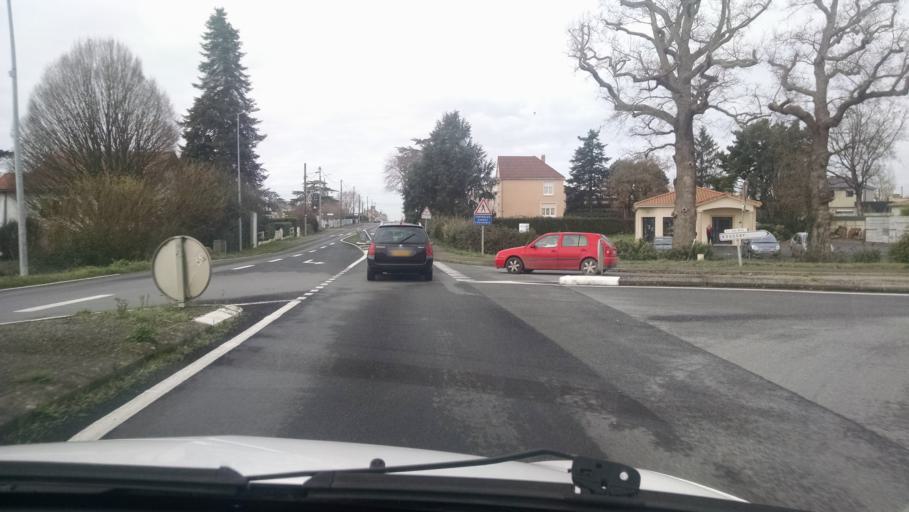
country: FR
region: Pays de la Loire
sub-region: Departement de Maine-et-Loire
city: Torfou
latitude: 47.0357
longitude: -1.1089
